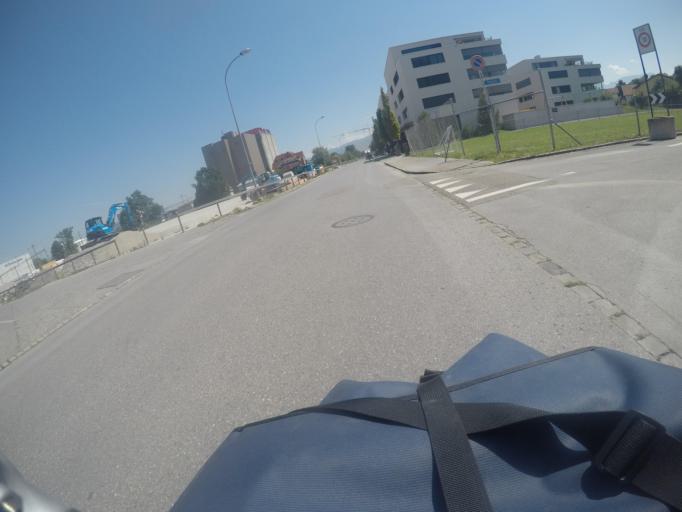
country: CH
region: Saint Gallen
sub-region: Wahlkreis Rheintal
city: Sankt Margrethen
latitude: 47.4514
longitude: 9.6415
